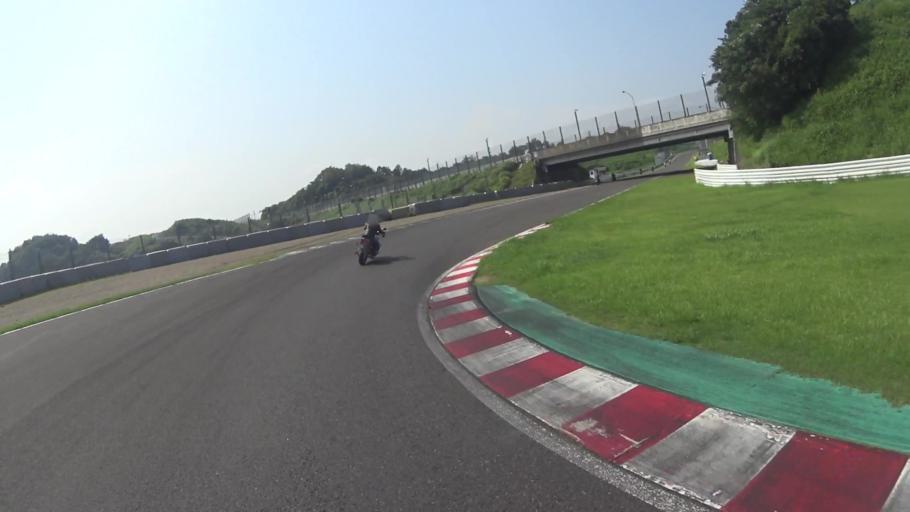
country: JP
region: Mie
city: Kawage
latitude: 34.8442
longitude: 136.5338
